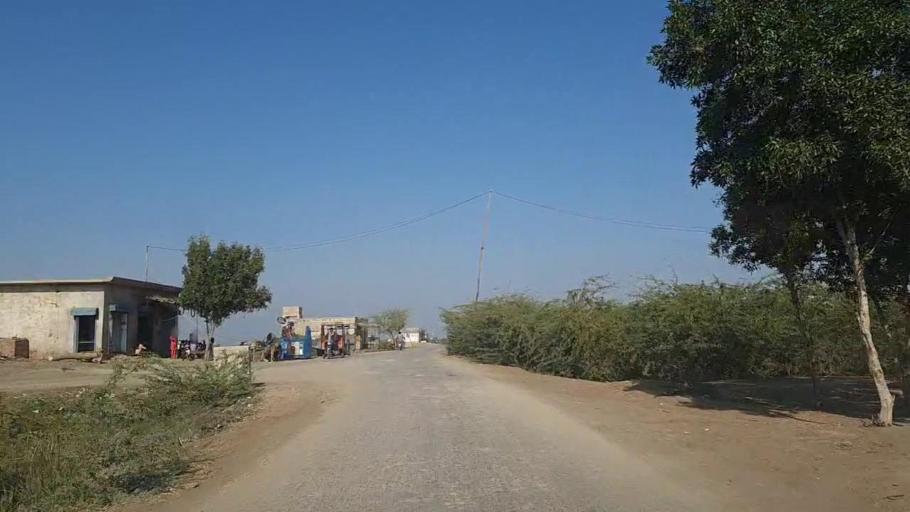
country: PK
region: Sindh
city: Digri
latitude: 25.0774
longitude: 69.2196
